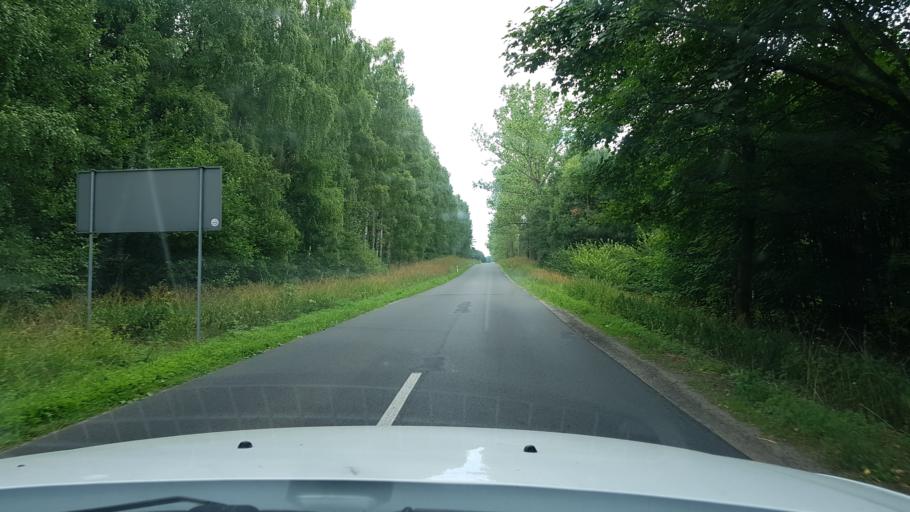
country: PL
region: West Pomeranian Voivodeship
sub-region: Powiat drawski
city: Wierzchowo
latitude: 53.4493
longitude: 16.0791
